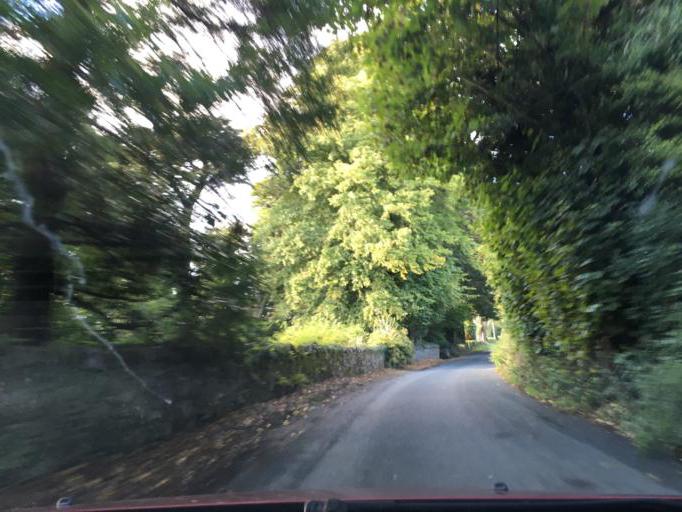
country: IE
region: Leinster
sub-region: Wicklow
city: Wicklow
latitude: 52.9153
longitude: -6.0809
